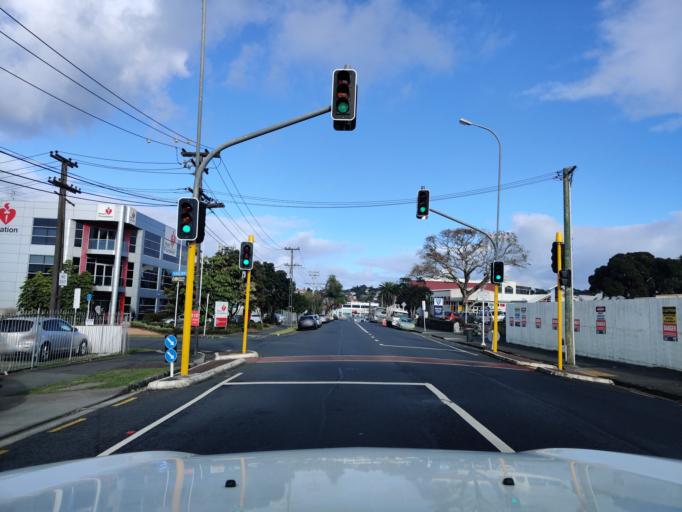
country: NZ
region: Auckland
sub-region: Auckland
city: Auckland
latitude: -36.8982
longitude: 174.8071
